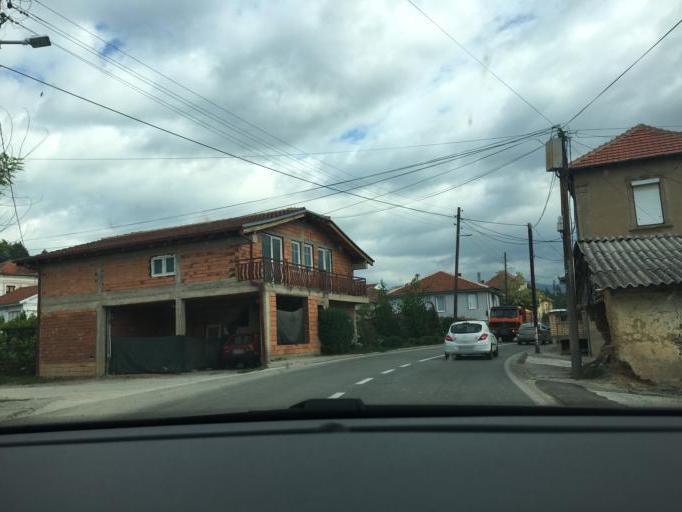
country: MK
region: Resen
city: Jankovec
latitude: 41.1089
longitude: 21.0115
